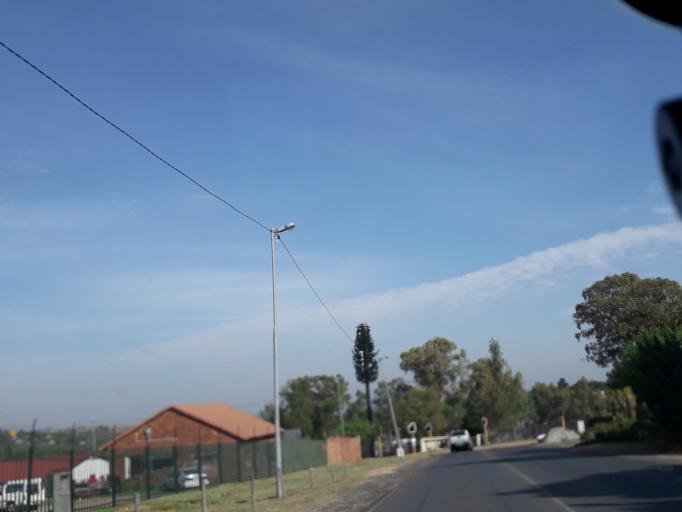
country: ZA
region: Gauteng
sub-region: West Rand District Municipality
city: Muldersdriseloop
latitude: -26.0713
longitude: 27.8909
